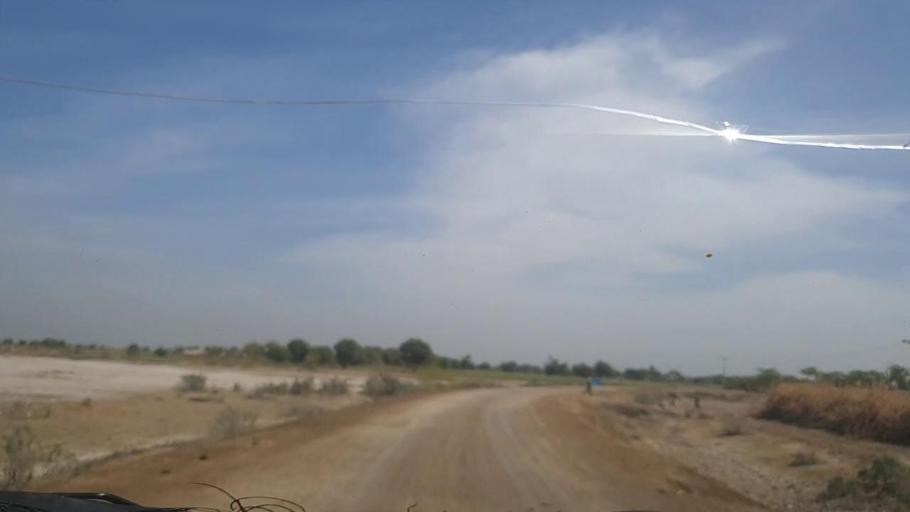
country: PK
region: Sindh
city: Dhoro Naro
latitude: 25.5024
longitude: 69.4761
